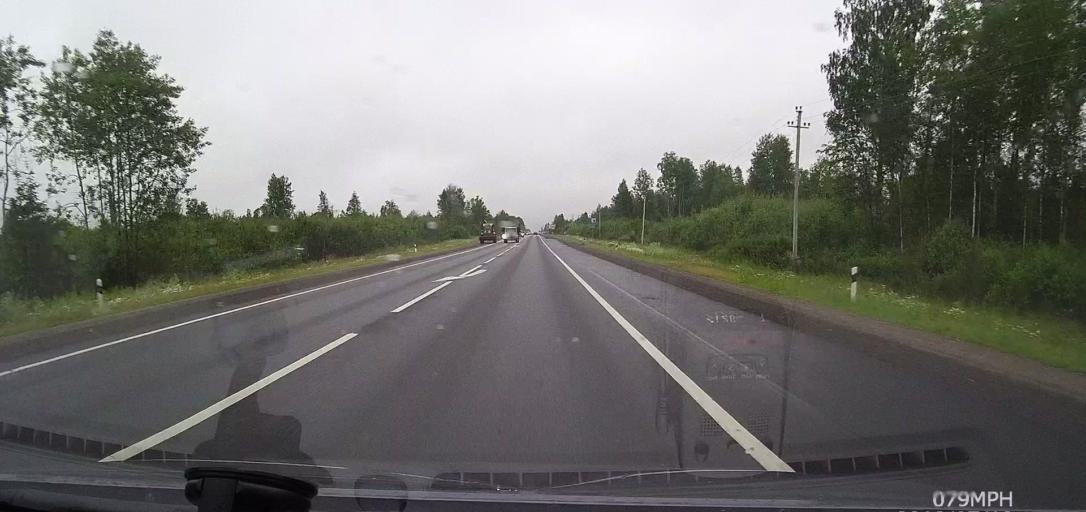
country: RU
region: Leningrad
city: Staraya Ladoga
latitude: 60.0016
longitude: 32.1168
